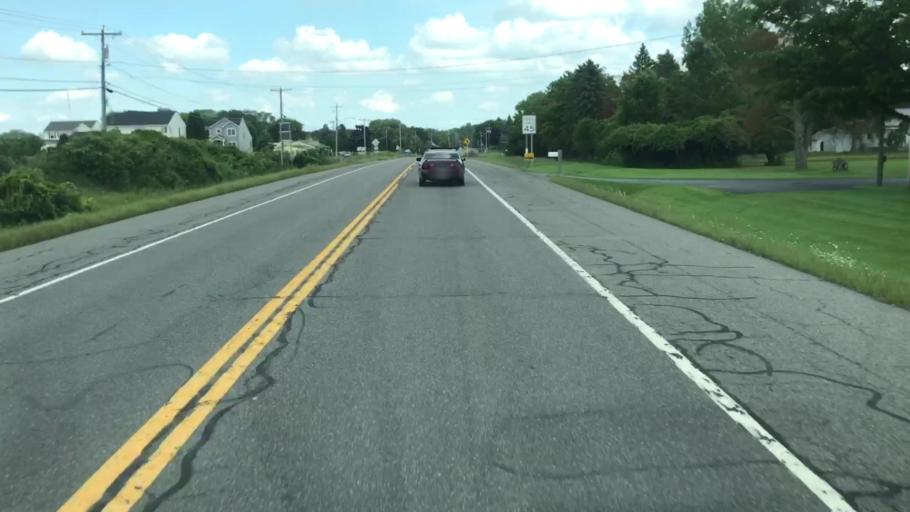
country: US
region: New York
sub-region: Onondaga County
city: Westvale
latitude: 42.9970
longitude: -76.2069
